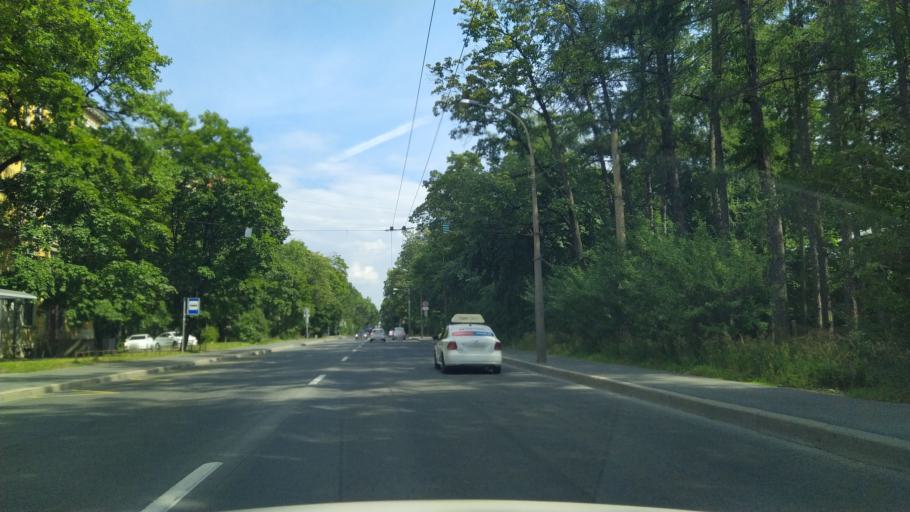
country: RU
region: Leningrad
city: Sampsonievskiy
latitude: 59.9964
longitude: 30.3420
